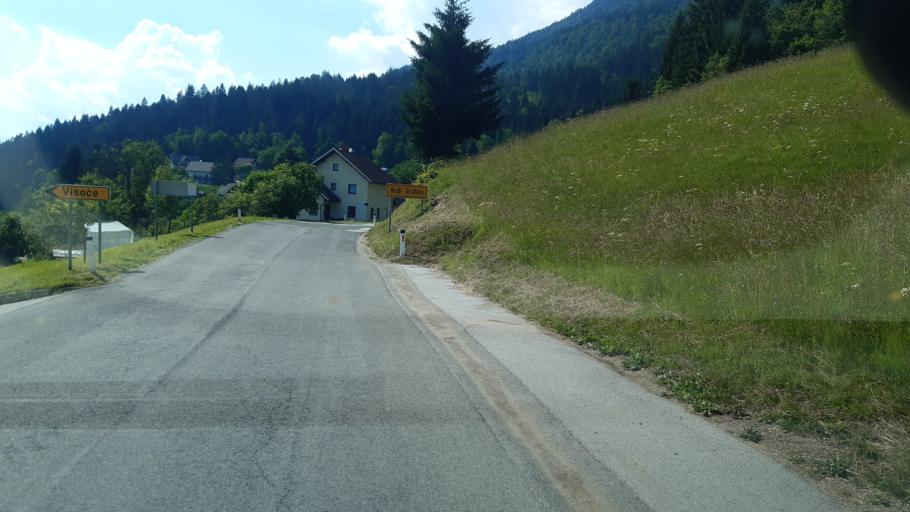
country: SI
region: Trzic
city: Bistrica pri Trzicu
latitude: 46.3593
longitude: 14.2649
